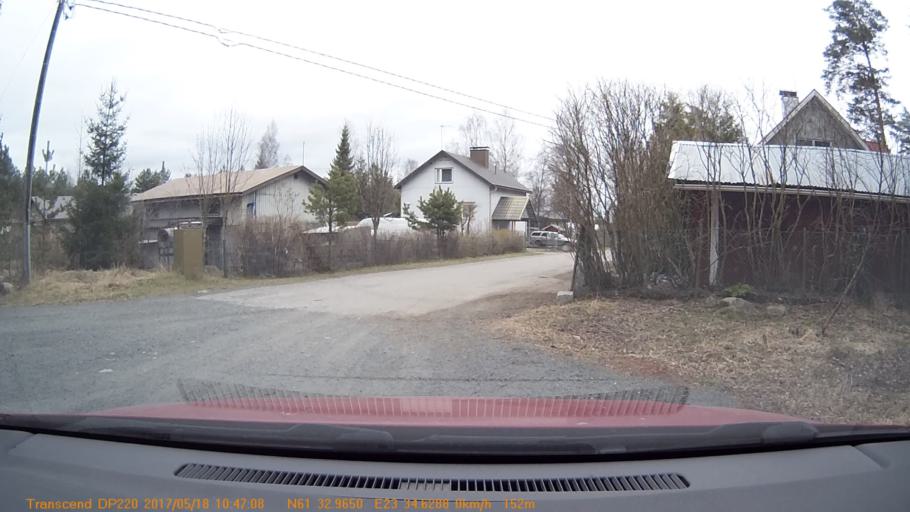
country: FI
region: Pirkanmaa
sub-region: Tampere
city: Yloejaervi
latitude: 61.5494
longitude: 23.5772
